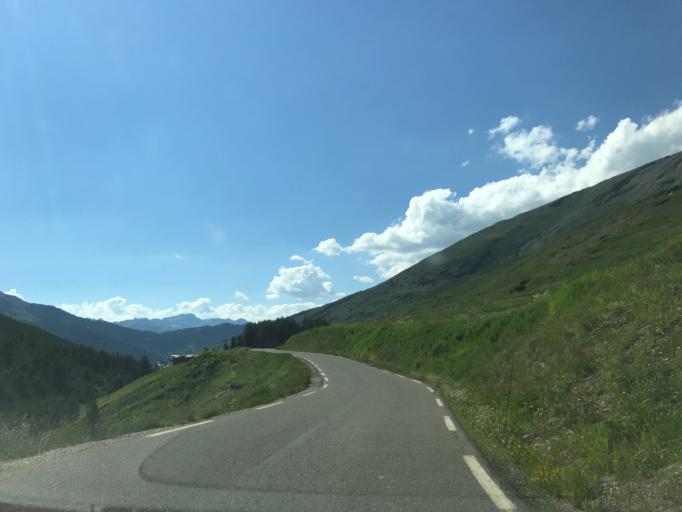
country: IT
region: Piedmont
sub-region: Provincia di Cuneo
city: Pontechianale
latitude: 44.7202
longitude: 6.8949
